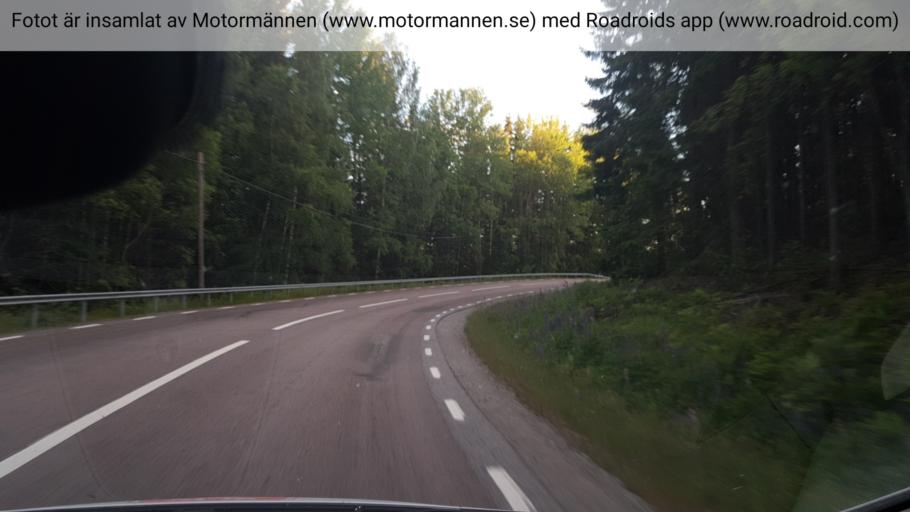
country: SE
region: Vaermland
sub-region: Sunne Kommun
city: Sunne
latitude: 59.6693
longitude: 13.0188
